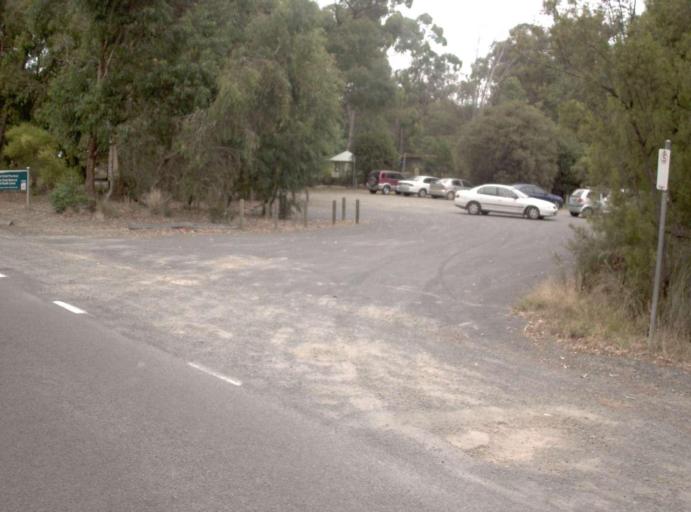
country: AU
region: Victoria
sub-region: Yarra Ranges
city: Badger Creek
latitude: -37.6804
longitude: 145.5325
